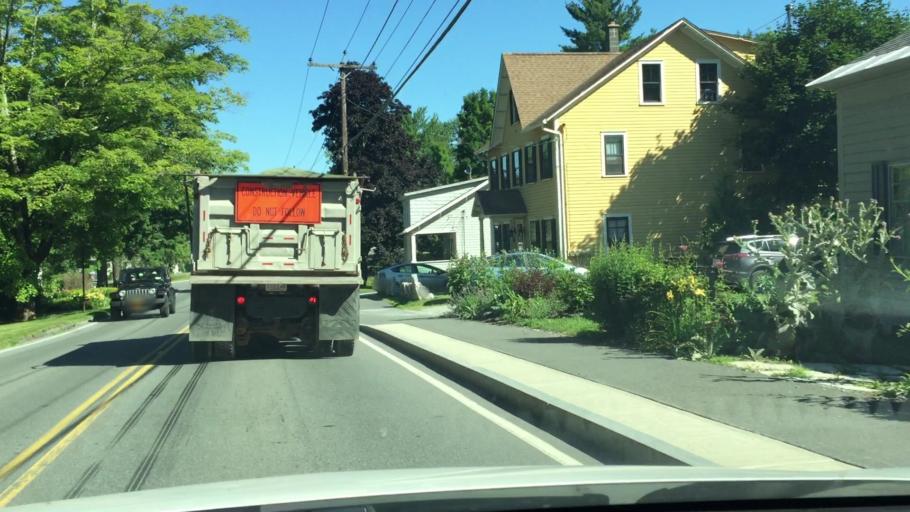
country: US
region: Massachusetts
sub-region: Berkshire County
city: West Stockbridge
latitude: 42.3315
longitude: -73.3659
